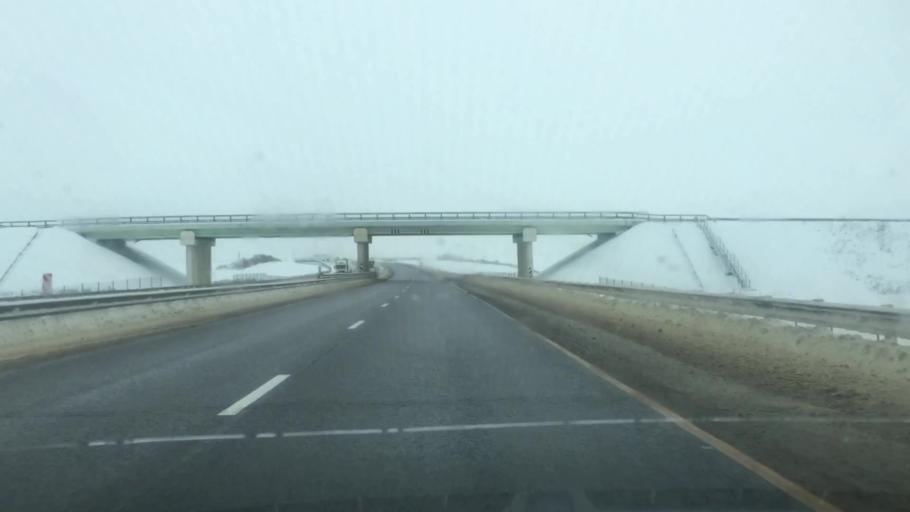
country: RU
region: Tula
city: Yefremov
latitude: 53.2257
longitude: 38.2082
